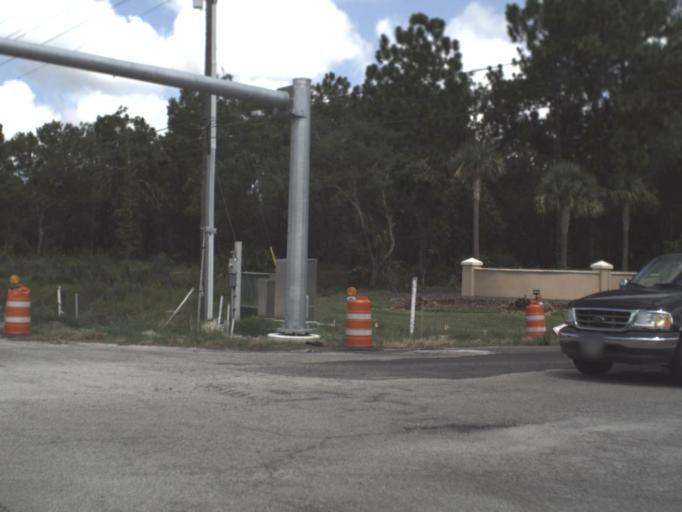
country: US
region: Florida
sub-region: Hernando County
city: High Point
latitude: 28.5333
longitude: -82.5345
